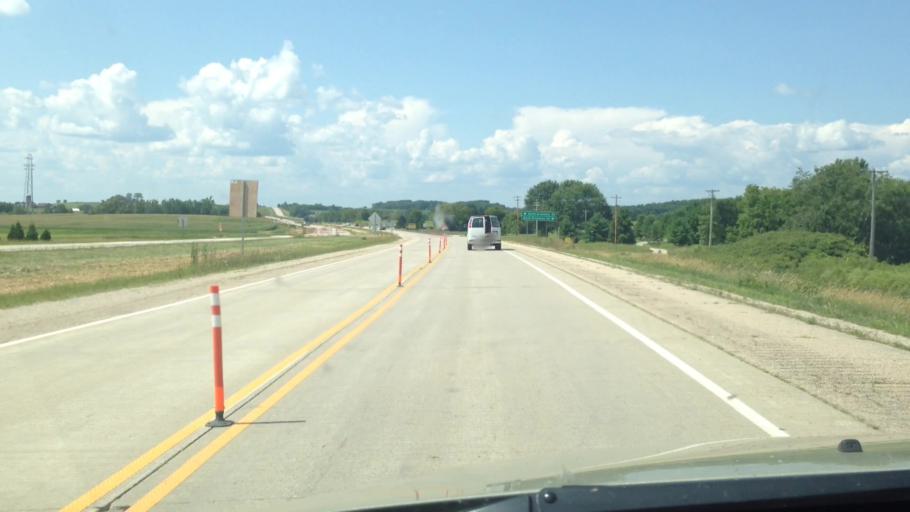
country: US
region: Wisconsin
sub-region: Shawano County
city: Bonduel
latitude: 44.7101
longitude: -88.3811
